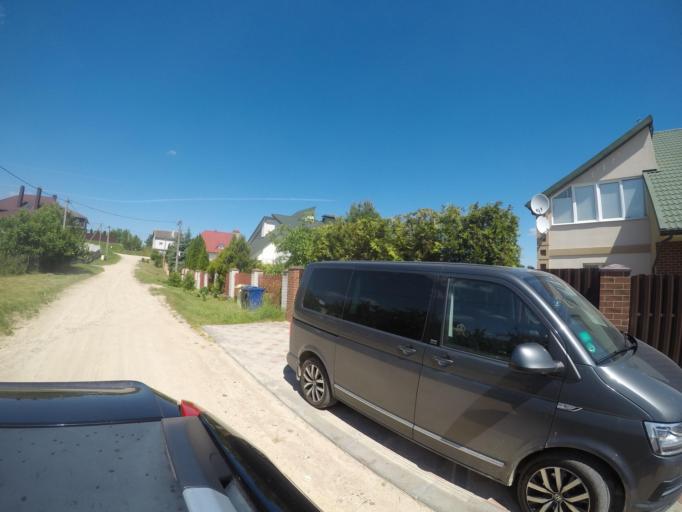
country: BY
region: Grodnenskaya
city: Hrodna
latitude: 53.7219
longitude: 23.8517
